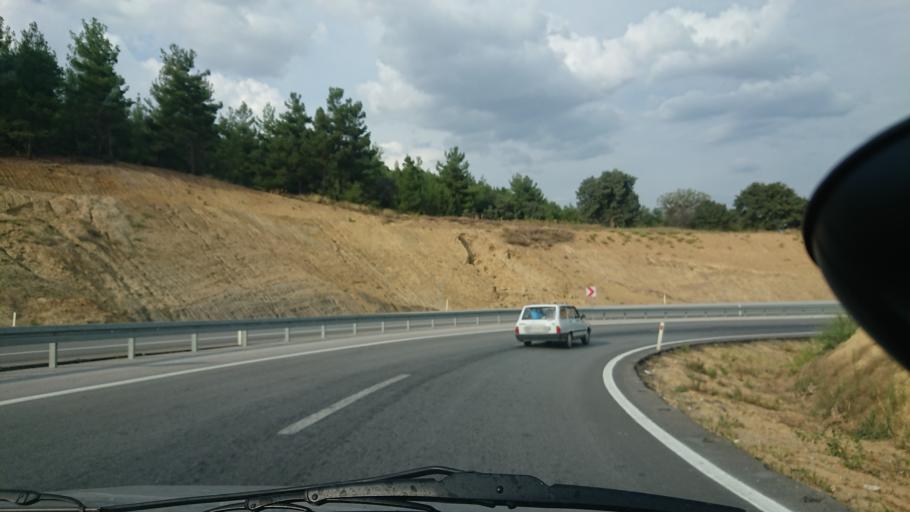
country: TR
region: Kuetahya
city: Gediz
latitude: 38.9357
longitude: 29.3097
